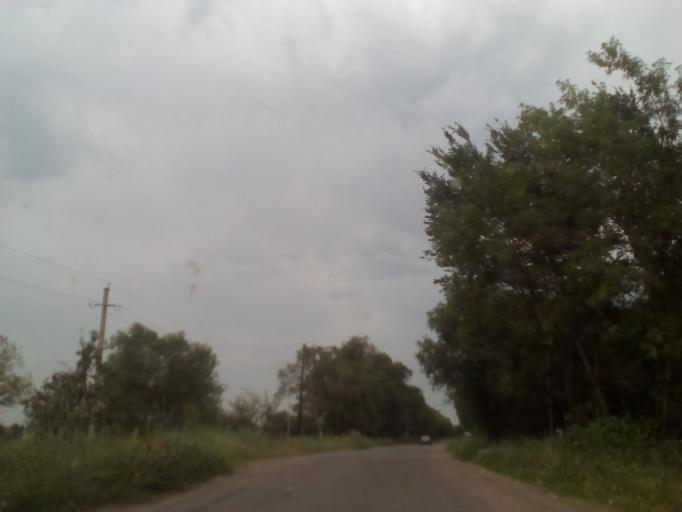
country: KZ
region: Almaty Oblysy
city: Burunday
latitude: 43.1639
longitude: 76.3848
